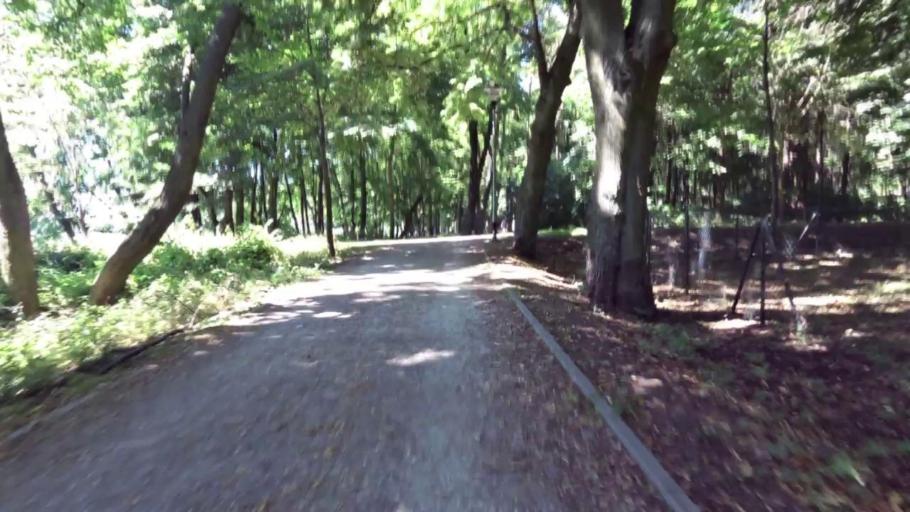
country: PL
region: West Pomeranian Voivodeship
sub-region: Powiat szczecinecki
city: Szczecinek
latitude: 53.7152
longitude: 16.6626
